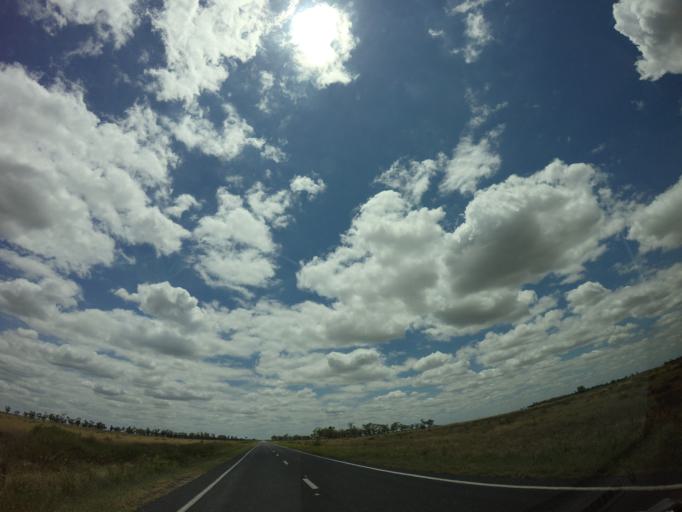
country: AU
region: New South Wales
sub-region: Moree Plains
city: Boggabilla
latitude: -28.6878
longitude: 150.2972
